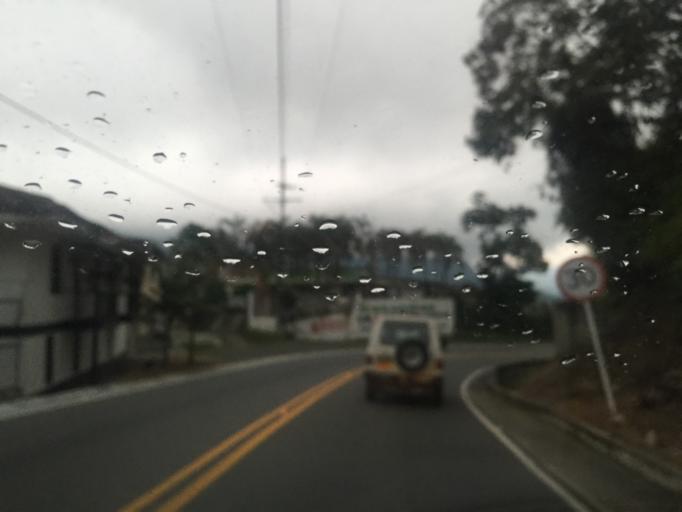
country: CO
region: Caldas
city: Villamaria
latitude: 5.0138
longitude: -75.5451
